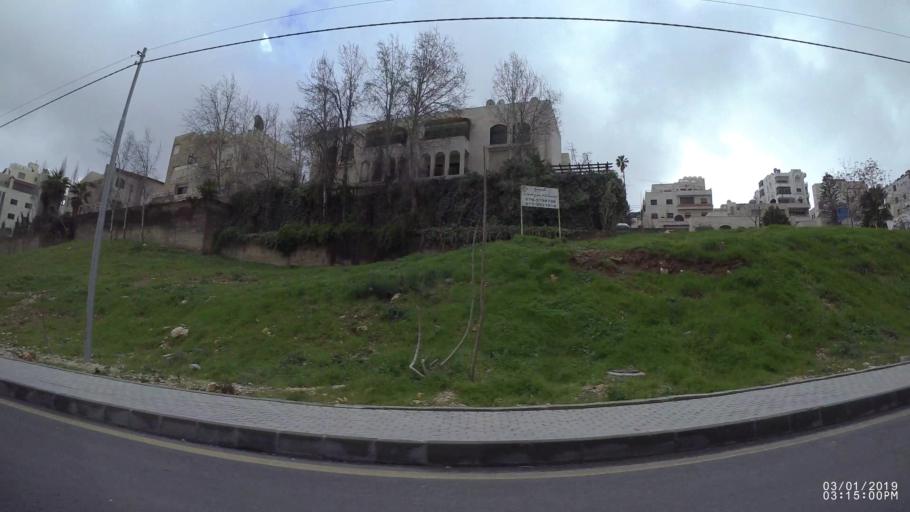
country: JO
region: Amman
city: Amman
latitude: 31.9532
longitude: 35.8893
